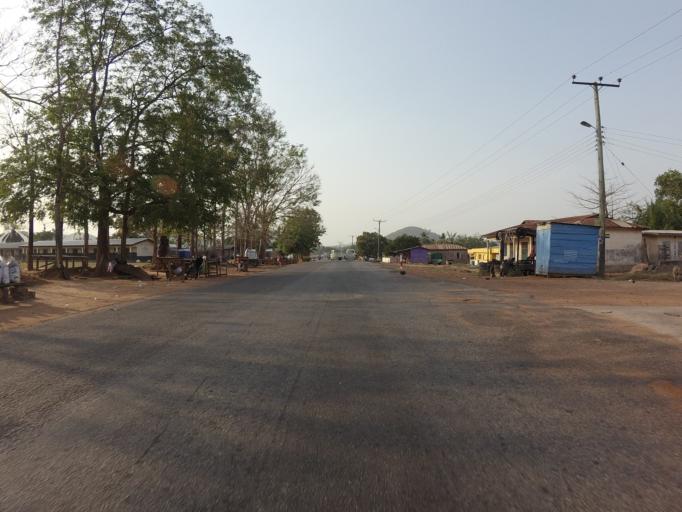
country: GH
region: Volta
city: Ho
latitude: 6.4052
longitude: 0.1758
